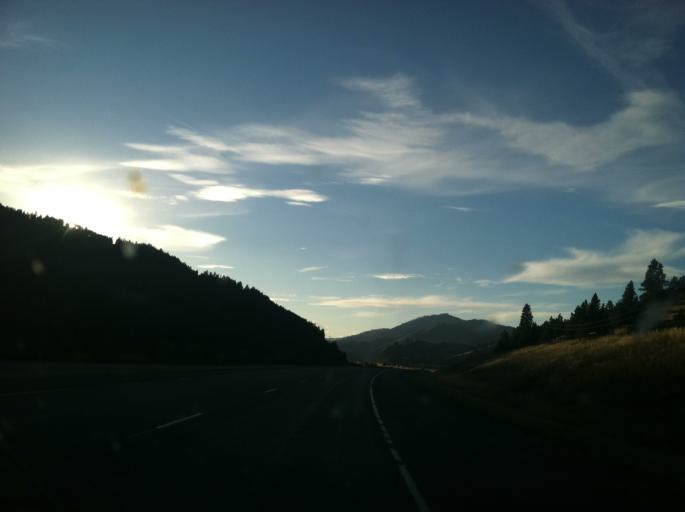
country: US
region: Montana
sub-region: Missoula County
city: Clinton
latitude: 46.7133
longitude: -113.5223
